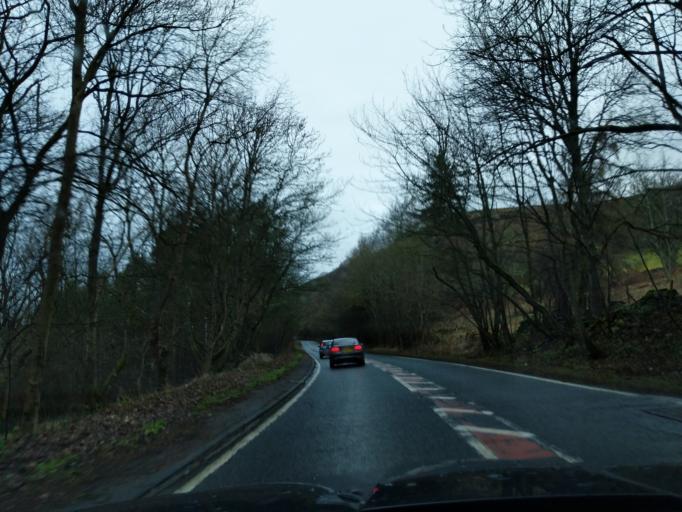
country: GB
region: Scotland
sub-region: The Scottish Borders
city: Galashiels
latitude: 55.6384
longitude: -2.8278
